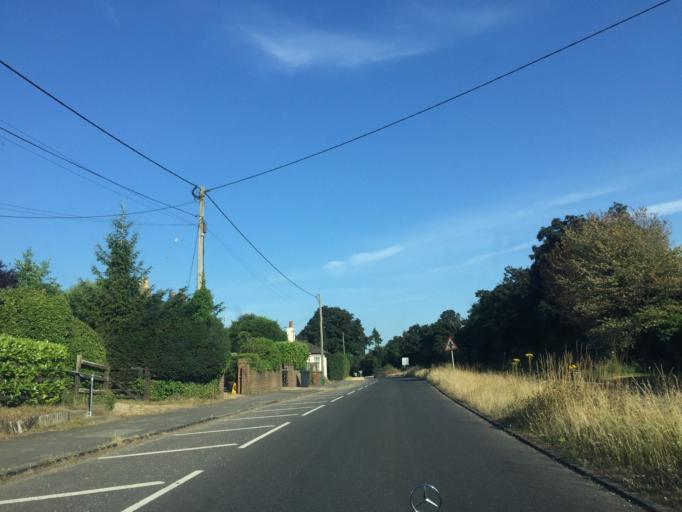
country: GB
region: England
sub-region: Oxfordshire
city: Rotherfield Peppard
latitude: 51.5616
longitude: -0.9543
